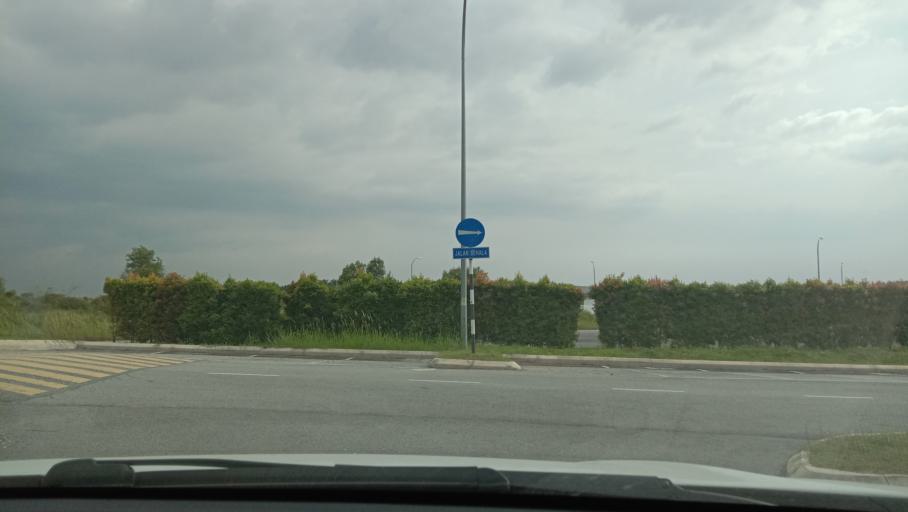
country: MY
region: Selangor
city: Ladang Seri Kundang
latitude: 3.2437
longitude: 101.4765
